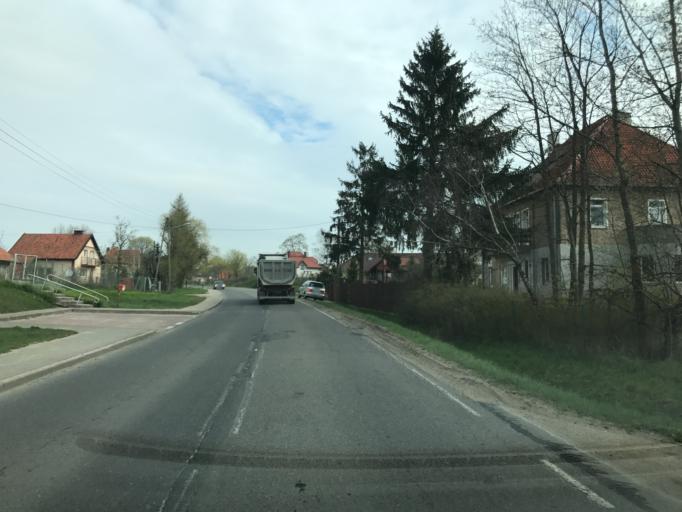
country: PL
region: Warmian-Masurian Voivodeship
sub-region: Powiat ostrodzki
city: Gierzwald
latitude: 53.5369
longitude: 20.0890
